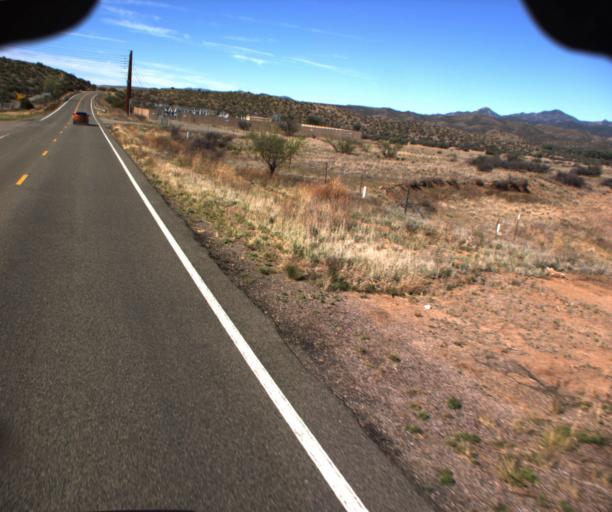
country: US
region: Arizona
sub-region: Yavapai County
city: Prescott
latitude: 34.3669
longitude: -112.6674
